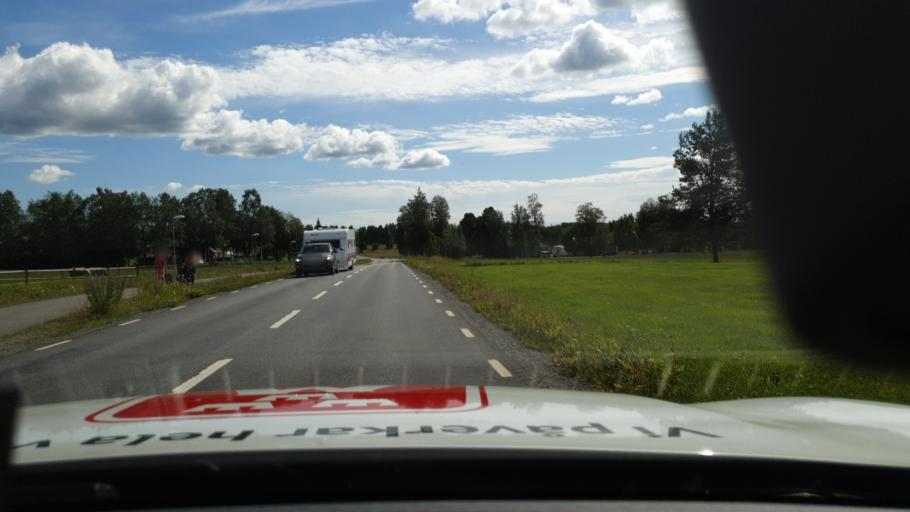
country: SE
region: Norrbotten
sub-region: Lulea Kommun
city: Sodra Sunderbyn
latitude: 65.8111
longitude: 22.0156
